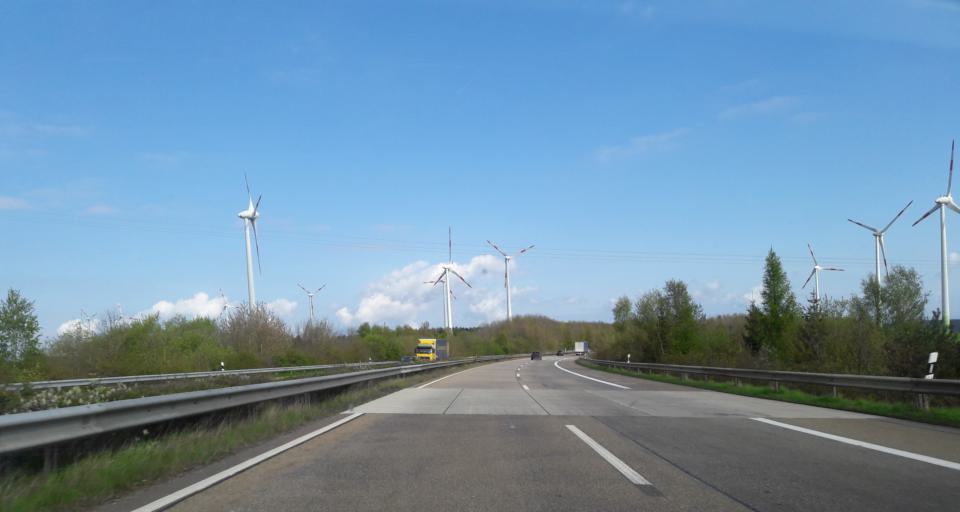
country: DE
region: Rheinland-Pfalz
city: Bescheid
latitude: 49.7439
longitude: 6.8753
